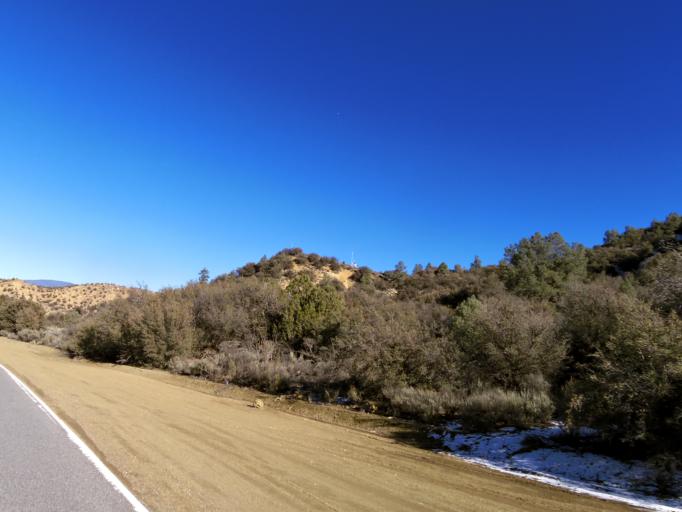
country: US
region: California
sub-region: Ventura County
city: Meiners Oaks
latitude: 34.6813
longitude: -119.3557
